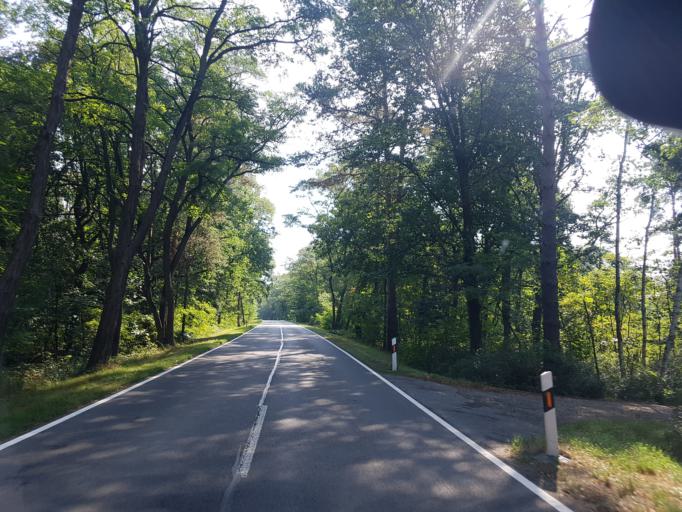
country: DE
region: Brandenburg
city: Lauchhammer
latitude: 51.5304
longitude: 13.6873
